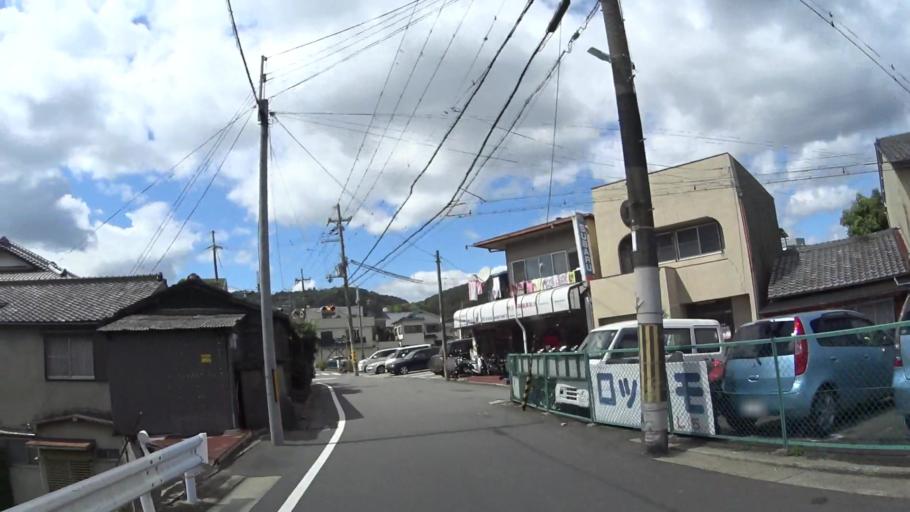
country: JP
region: Kyoto
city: Kyoto
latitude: 34.9874
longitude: 135.8045
